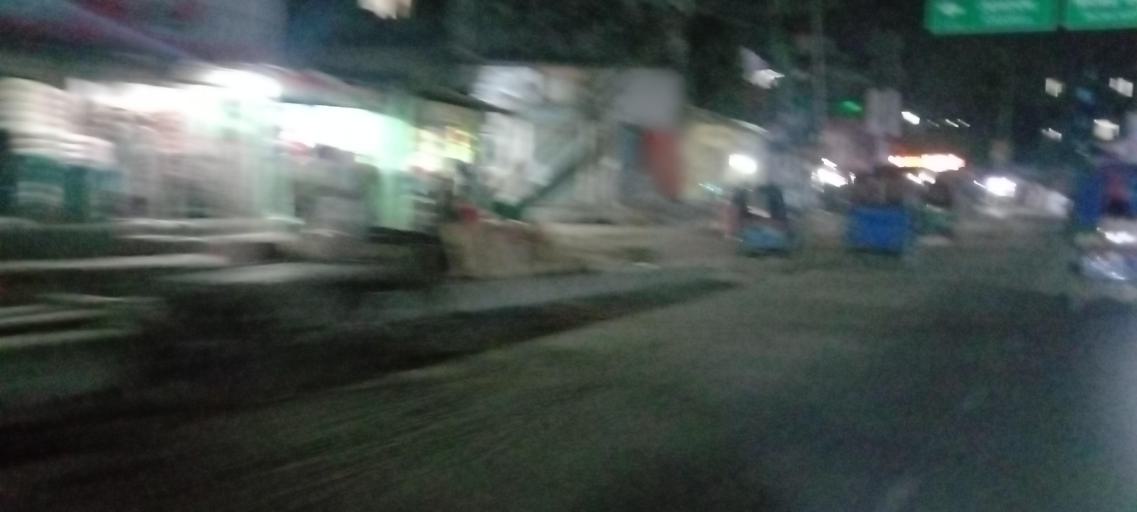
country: BD
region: Dhaka
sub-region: Dhaka
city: Dhaka
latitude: 23.7026
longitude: 90.3900
